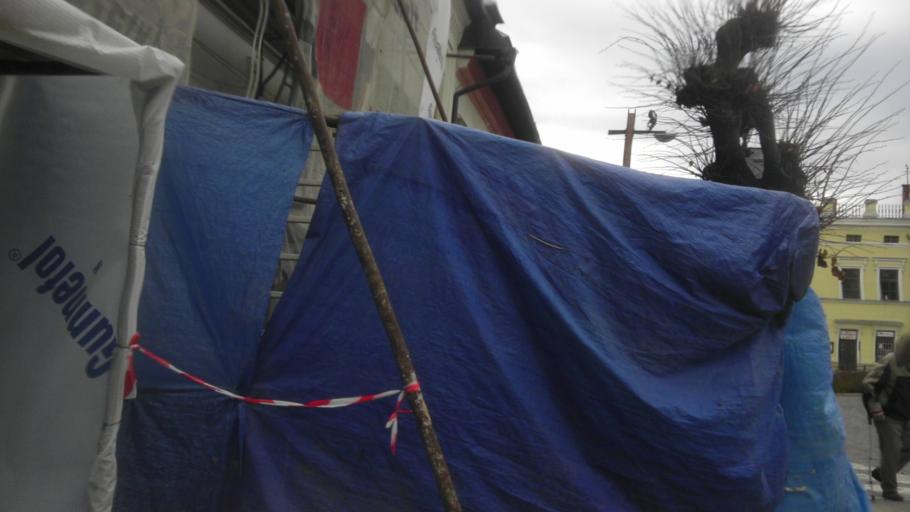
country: SK
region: Presovsky
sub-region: Okres Presov
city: Levoca
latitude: 49.0251
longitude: 20.5889
